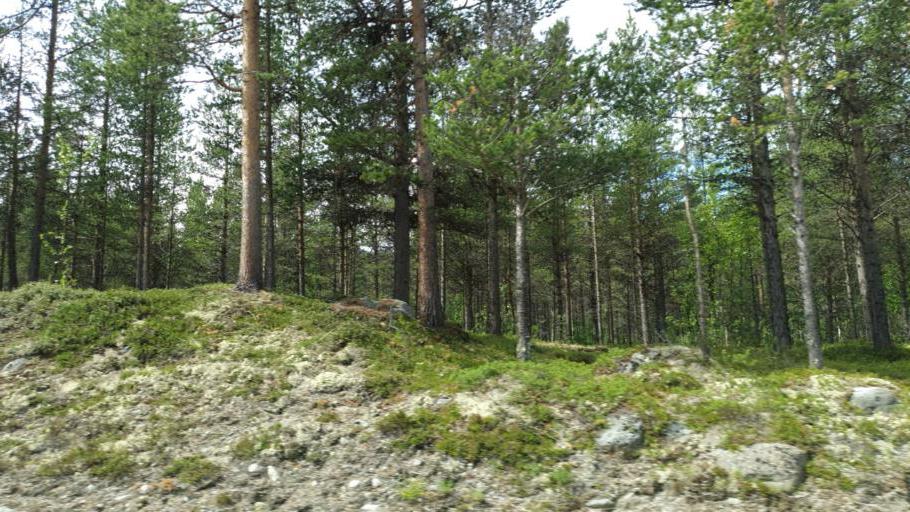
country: NO
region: Oppland
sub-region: Vaga
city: Vagamo
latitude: 61.6973
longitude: 9.0599
